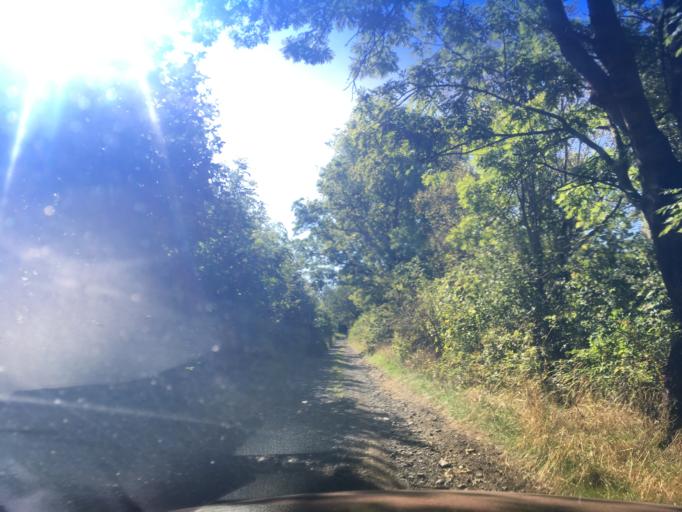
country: PL
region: Lower Silesian Voivodeship
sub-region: Powiat lubanski
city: Lesna
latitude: 51.0010
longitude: 15.1984
